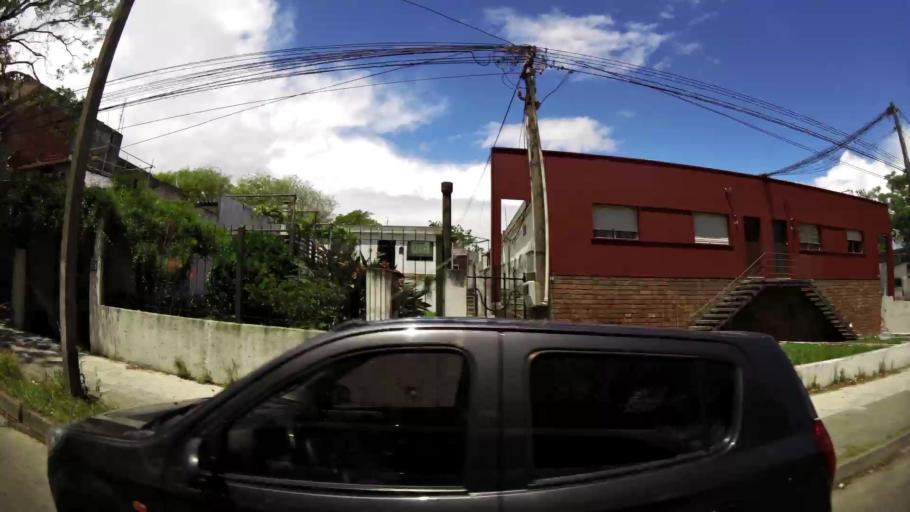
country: UY
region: Montevideo
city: Montevideo
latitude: -34.8488
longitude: -56.1771
